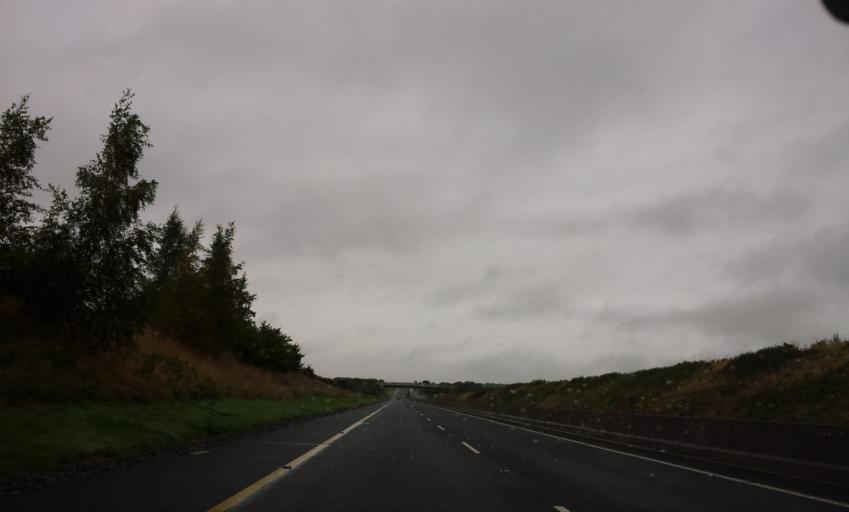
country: IE
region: Munster
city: Cashel
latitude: 52.4519
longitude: -7.9087
